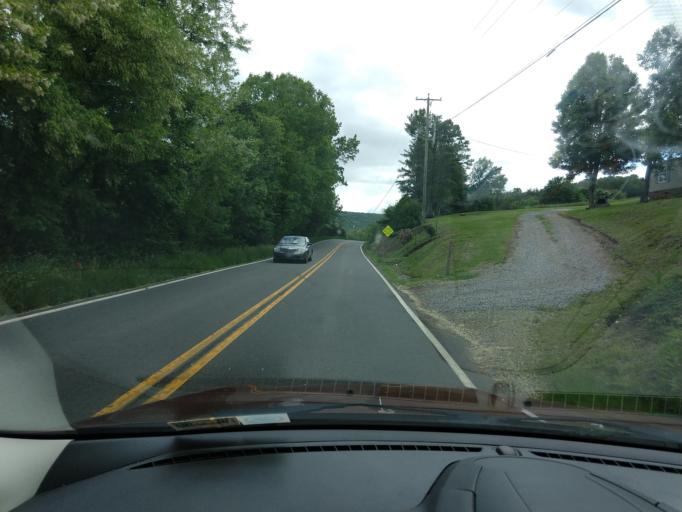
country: US
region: Virginia
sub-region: Wythe County
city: Wytheville
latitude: 36.9023
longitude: -80.9695
